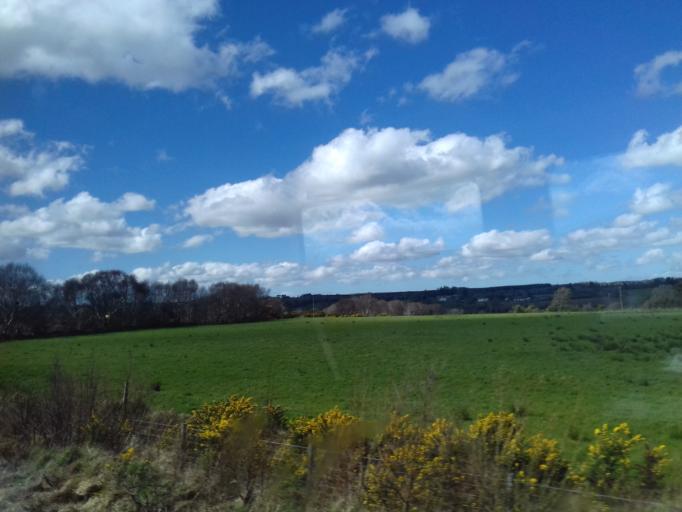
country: IE
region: Munster
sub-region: County Cork
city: Millstreet
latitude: 52.0771
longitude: -9.1652
